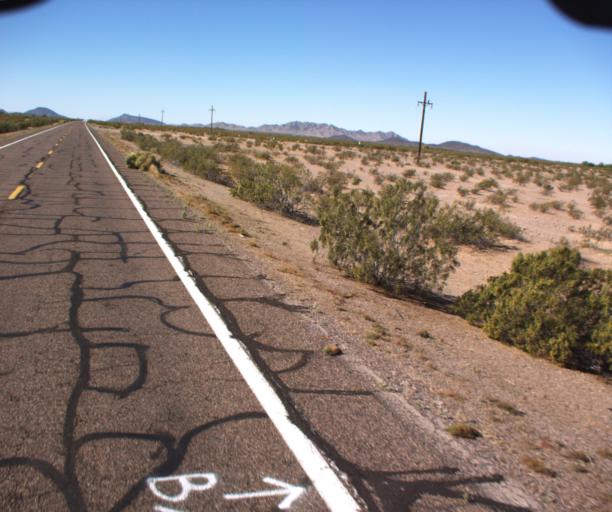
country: US
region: Arizona
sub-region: Maricopa County
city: Gila Bend
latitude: 32.8636
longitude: -112.7638
